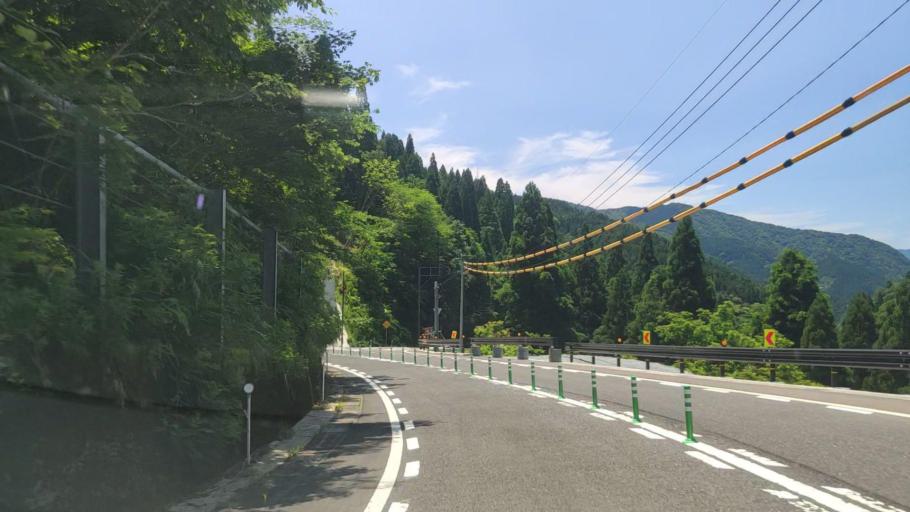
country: JP
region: Tottori
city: Tottori
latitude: 35.3554
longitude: 134.4732
